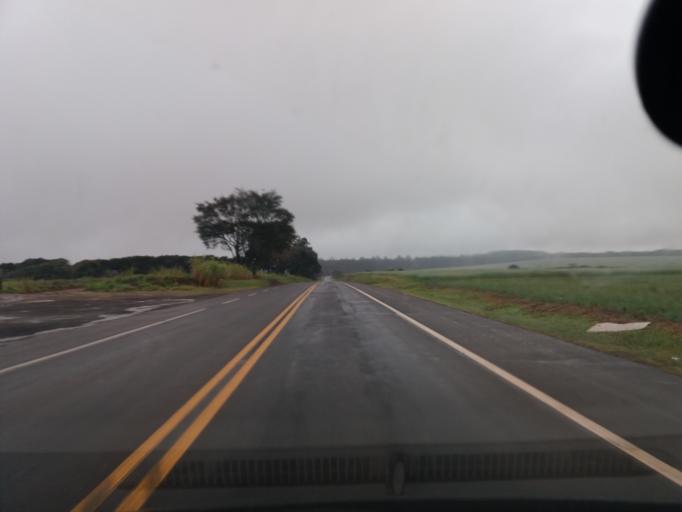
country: BR
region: Parana
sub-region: Campo Mourao
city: Campo Mourao
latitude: -24.2971
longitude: -52.5857
